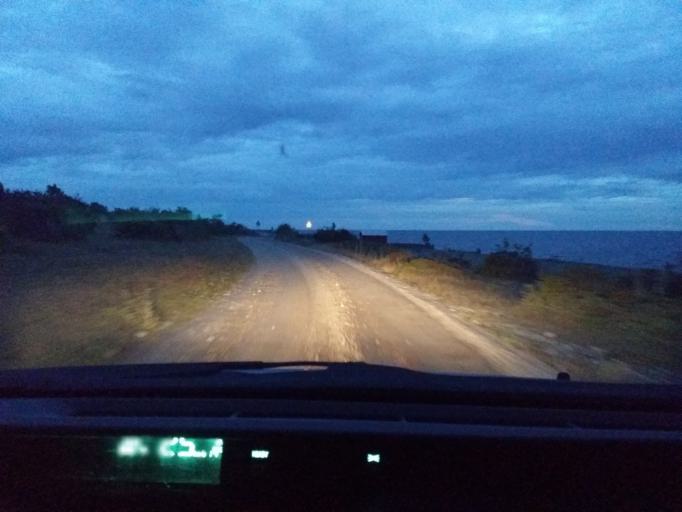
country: SE
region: Kalmar
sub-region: Borgholms Kommun
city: Borgholm
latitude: 57.1465
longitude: 16.9113
